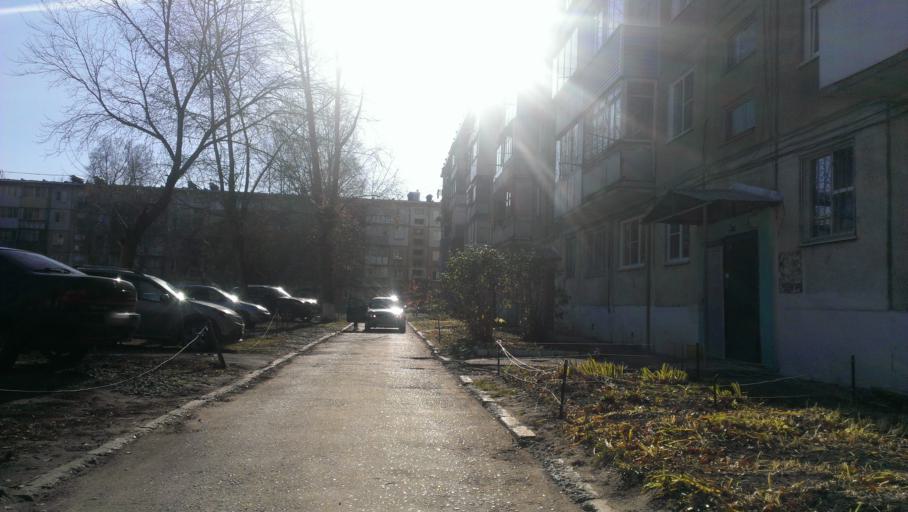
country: RU
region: Altai Krai
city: Novosilikatnyy
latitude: 53.3502
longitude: 83.6815
